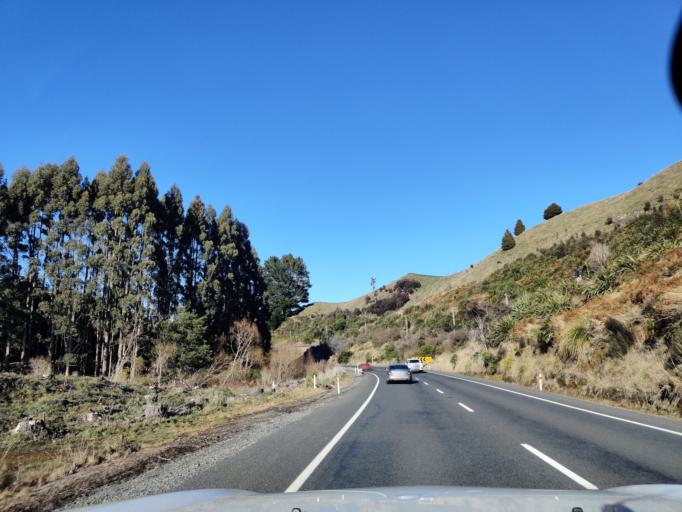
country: NZ
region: Manawatu-Wanganui
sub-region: Ruapehu District
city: Waiouru
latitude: -39.5631
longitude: 175.6983
